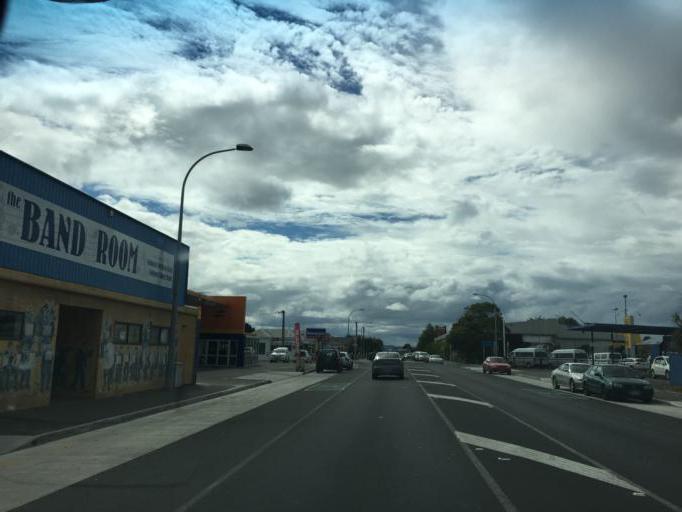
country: NZ
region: Gisborne
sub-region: Gisborne District
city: Gisborne
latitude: -38.6657
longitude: 178.0223
